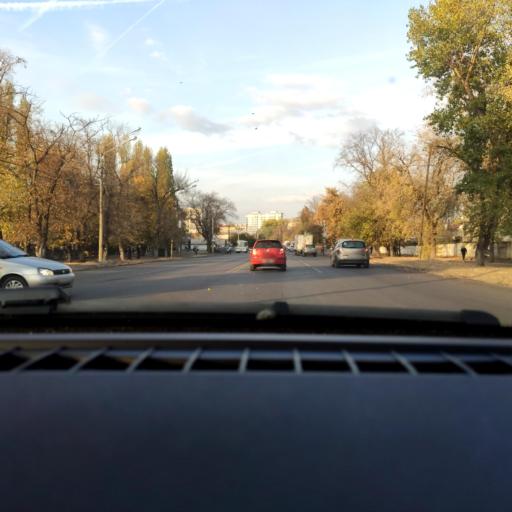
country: RU
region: Voronezj
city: Voronezh
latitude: 51.6562
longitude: 39.2743
